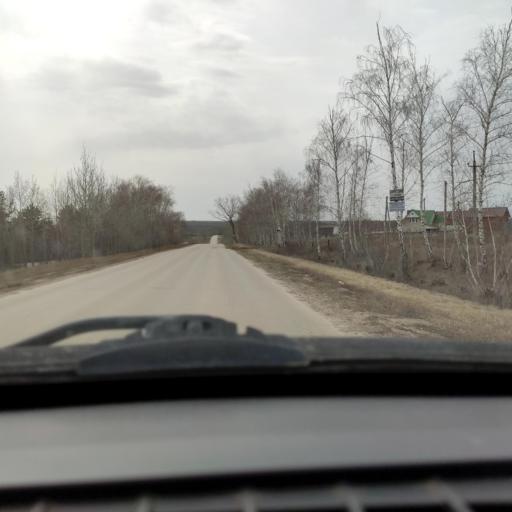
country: RU
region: Samara
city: Dubovyy Umet
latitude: 53.0442
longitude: 50.1814
